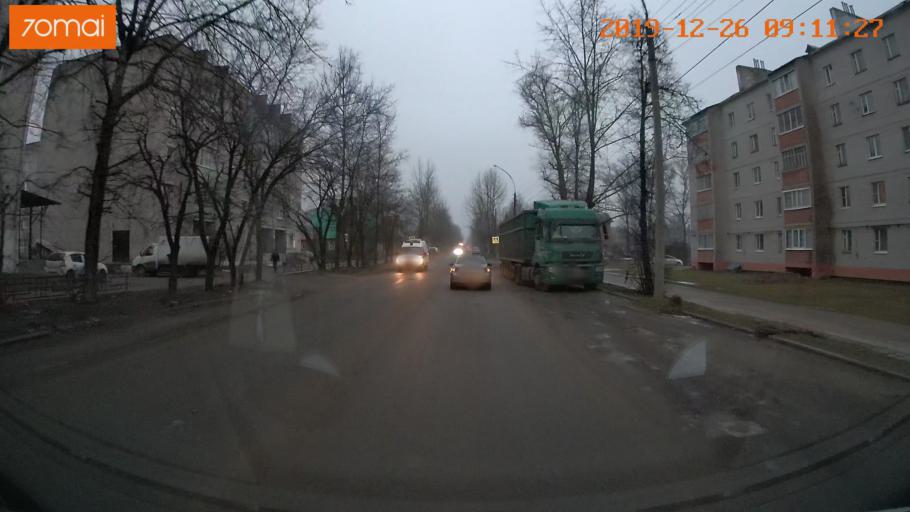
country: RU
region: Vologda
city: Gryazovets
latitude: 58.8763
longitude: 40.2527
